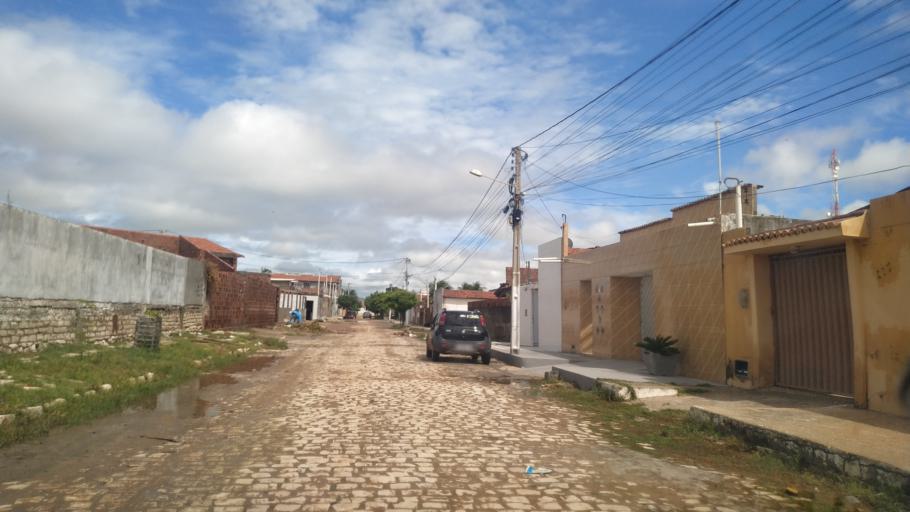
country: BR
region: Rio Grande do Norte
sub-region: Areia Branca
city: Areia Branca
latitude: -4.9543
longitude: -37.1244
